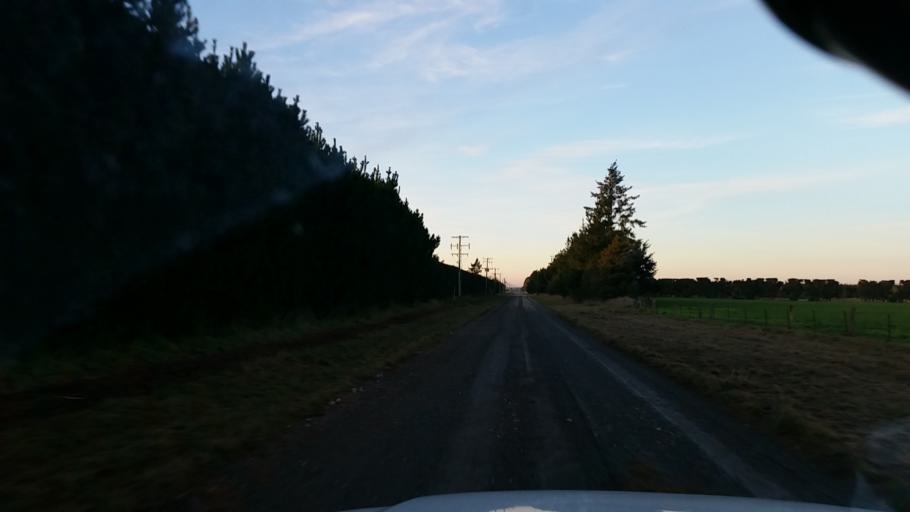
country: NZ
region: Canterbury
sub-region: Ashburton District
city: Methven
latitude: -43.7885
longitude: 171.5278
